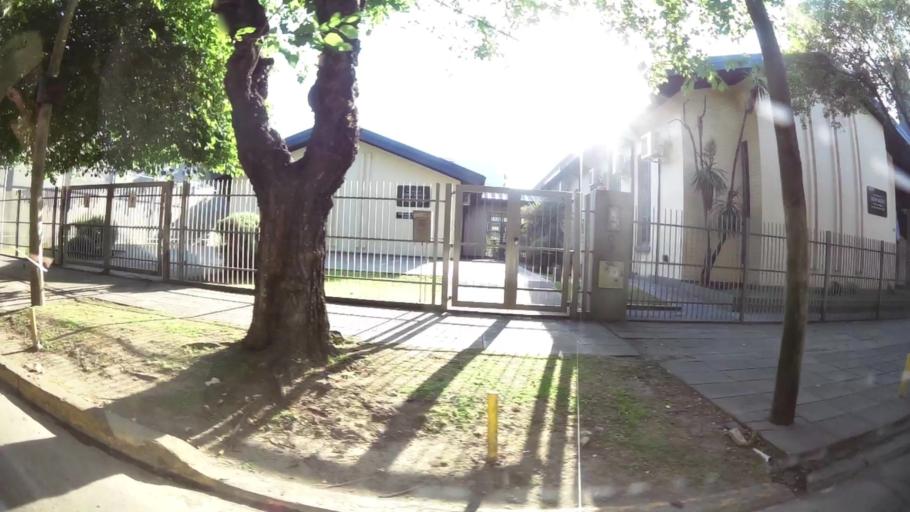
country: AR
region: Buenos Aires
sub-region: Partido de Merlo
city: Merlo
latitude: -34.6691
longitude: -58.7235
